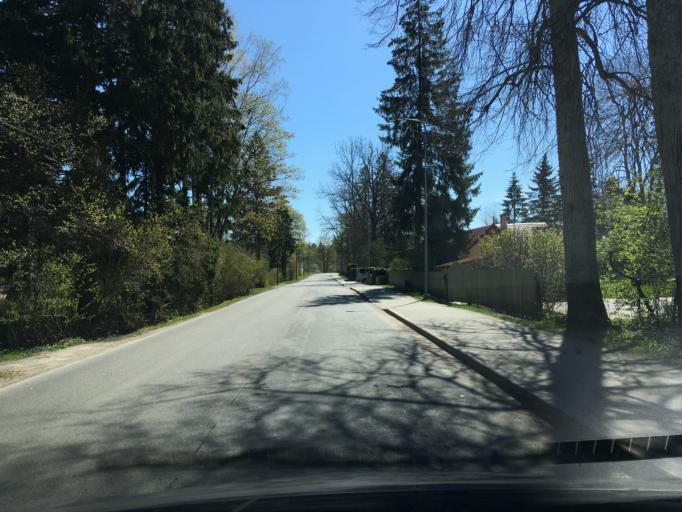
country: EE
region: Harju
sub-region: Raasiku vald
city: Arukula
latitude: 59.3682
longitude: 25.0800
